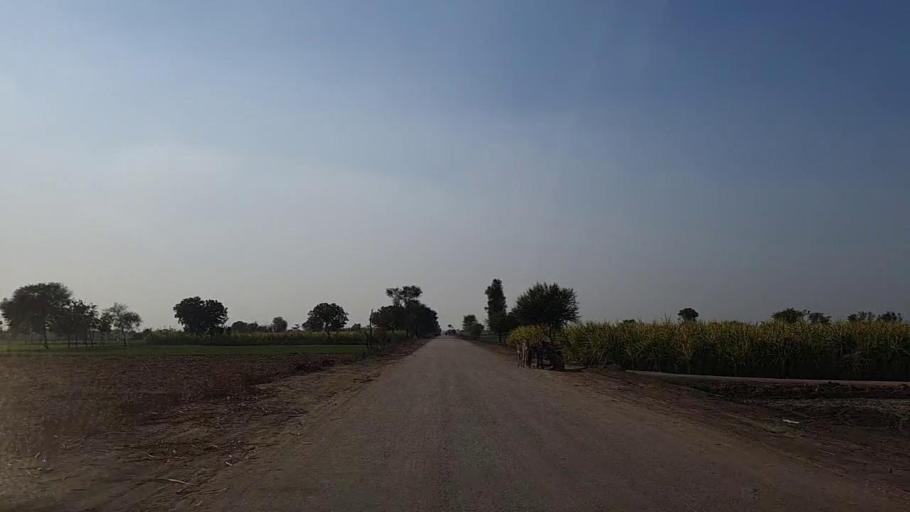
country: PK
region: Sindh
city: Daur
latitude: 26.4039
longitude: 68.2843
